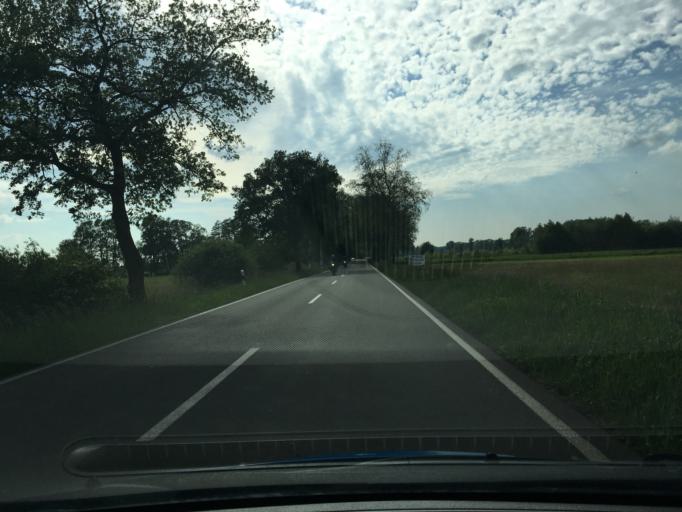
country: DE
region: Lower Saxony
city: Kalbe
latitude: 53.2792
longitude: 9.5941
